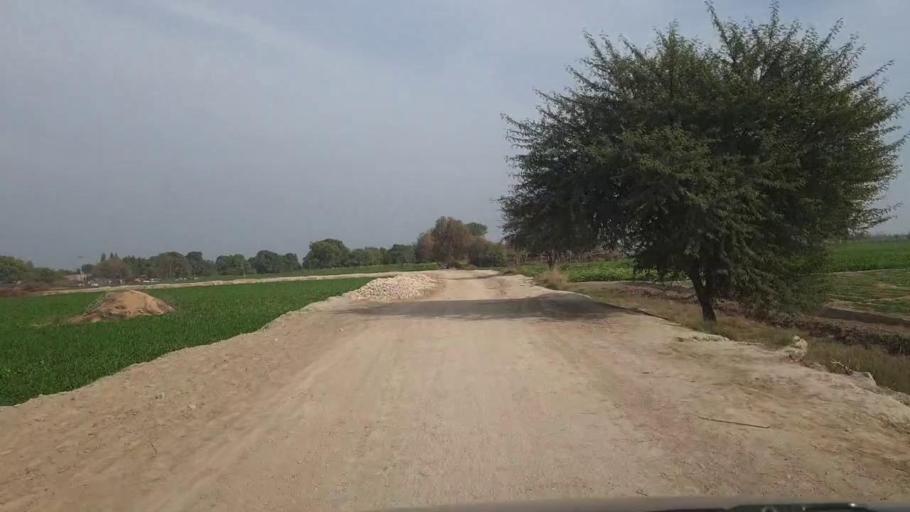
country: PK
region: Sindh
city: Shahpur Chakar
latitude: 26.0790
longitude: 68.5012
